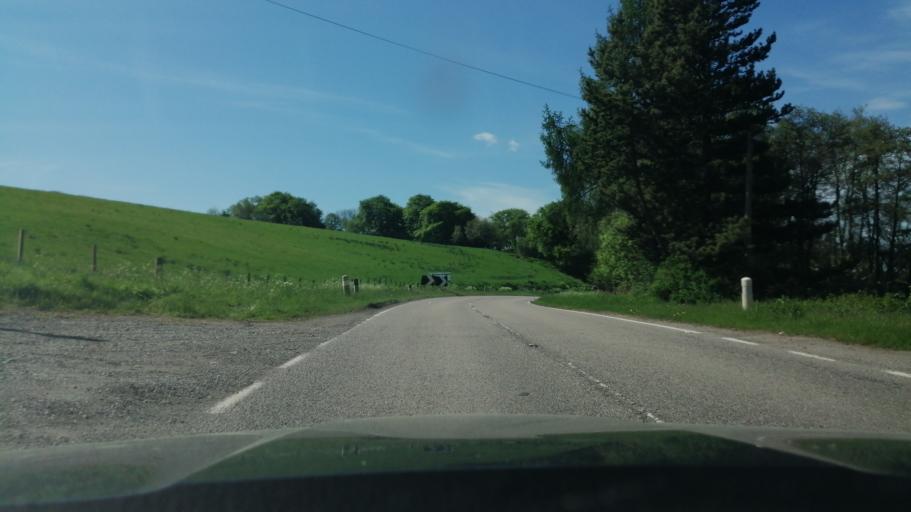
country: GB
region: Scotland
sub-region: Moray
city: Dufftown
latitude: 57.5039
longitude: -3.1296
